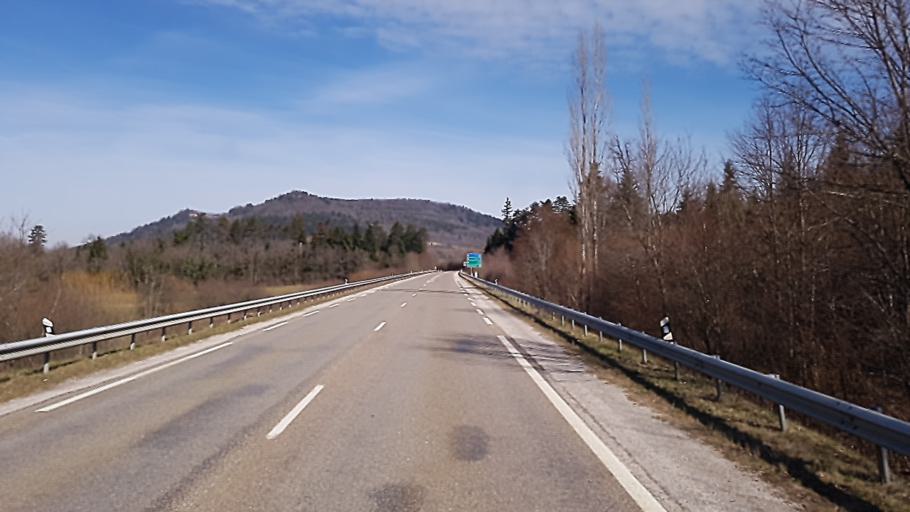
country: FR
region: Franche-Comte
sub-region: Departement du Jura
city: Champagnole
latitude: 46.7373
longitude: 5.9285
